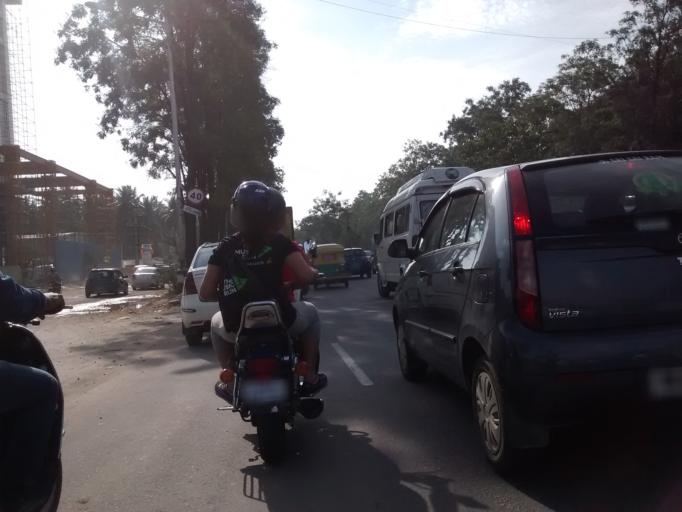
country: IN
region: Karnataka
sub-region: Bangalore Urban
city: Yelahanka
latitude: 13.0429
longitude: 77.6102
